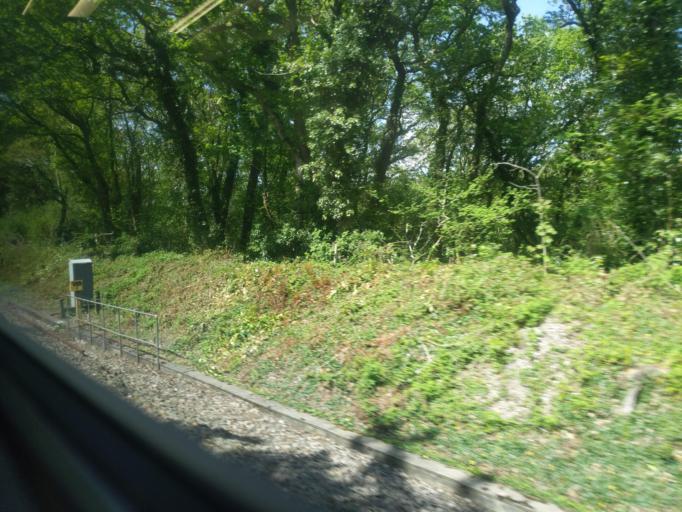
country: GB
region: England
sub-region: Cornwall
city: Liskeard
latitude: 50.4528
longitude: -4.5615
